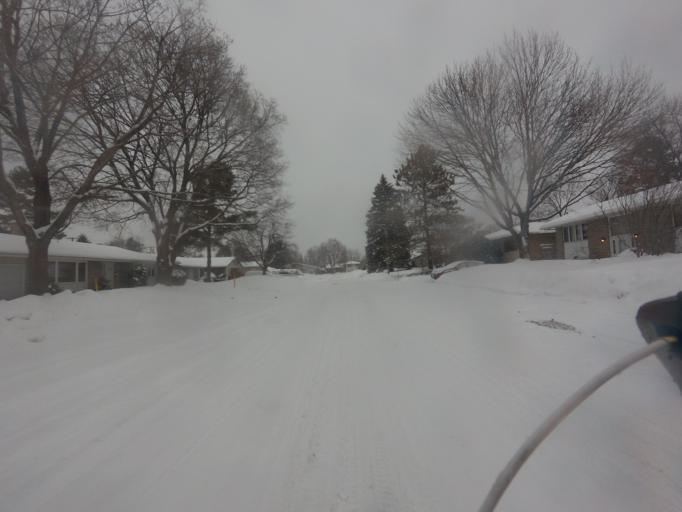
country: CA
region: Ontario
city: Ottawa
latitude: 45.3694
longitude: -75.6791
